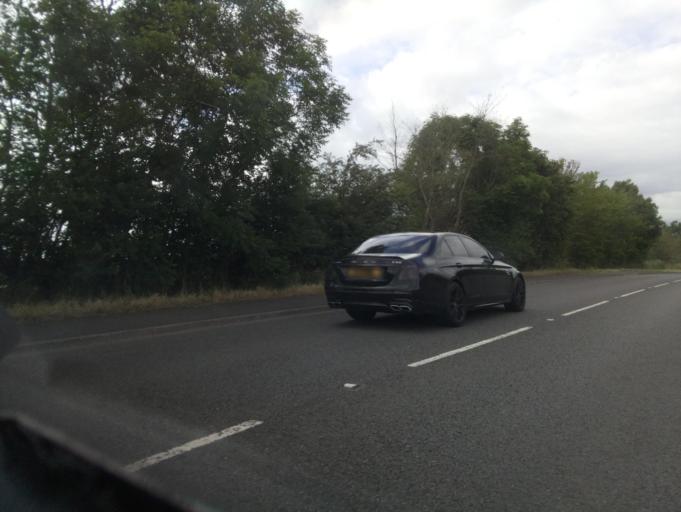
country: GB
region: England
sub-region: Dudley
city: Kingswinford
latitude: 52.4951
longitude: -2.1882
